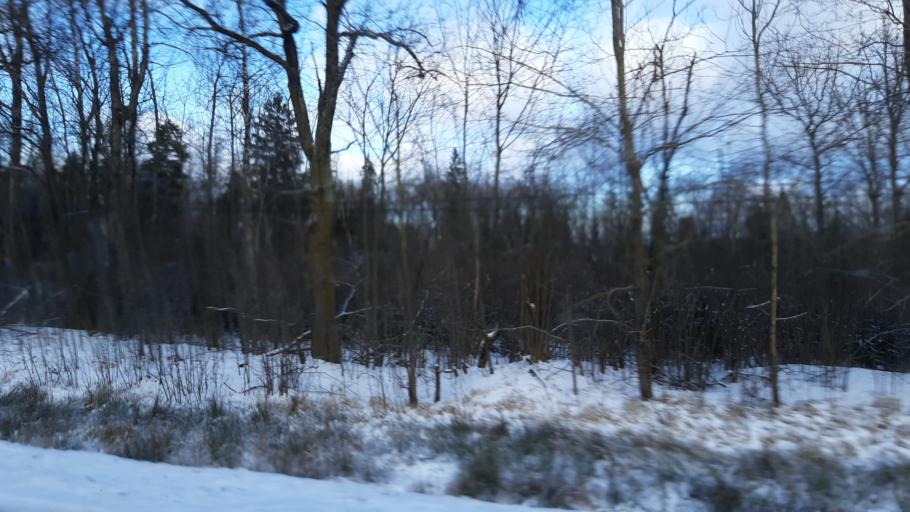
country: RU
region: Moskovskaya
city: Svatkovo
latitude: 56.3158
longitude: 38.3055
